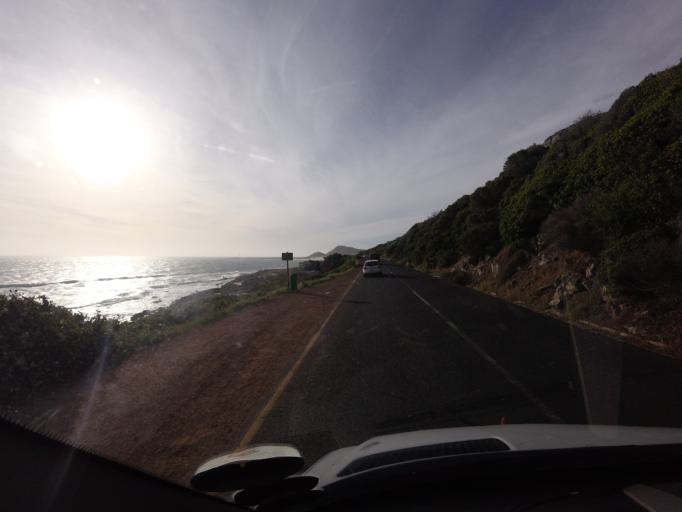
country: ZA
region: Western Cape
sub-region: City of Cape Town
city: Constantia
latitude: -34.1820
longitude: 18.3603
